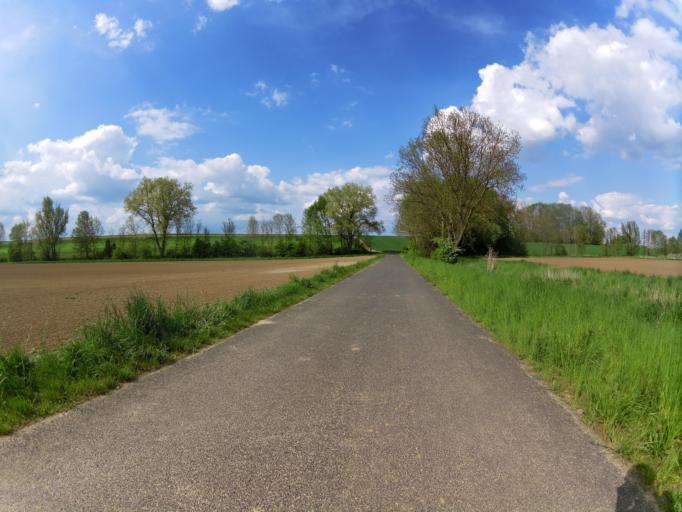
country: DE
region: Bavaria
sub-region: Regierungsbezirk Unterfranken
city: Giebelstadt
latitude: 49.6231
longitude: 9.9377
